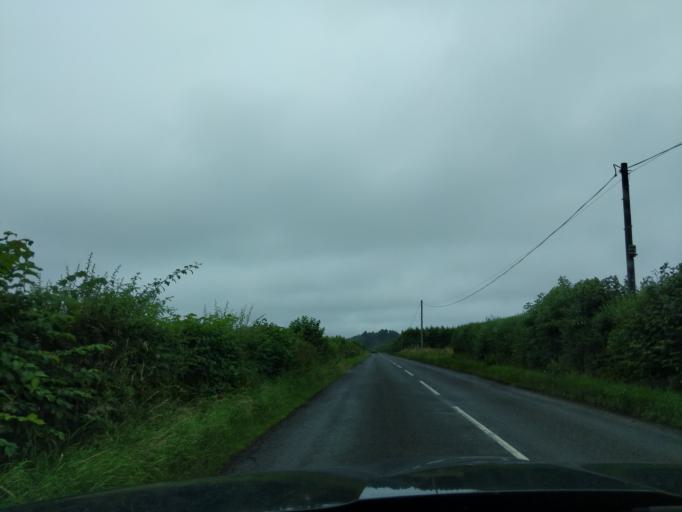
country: GB
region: England
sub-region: Northumberland
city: Lowick
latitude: 55.6488
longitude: -2.0001
